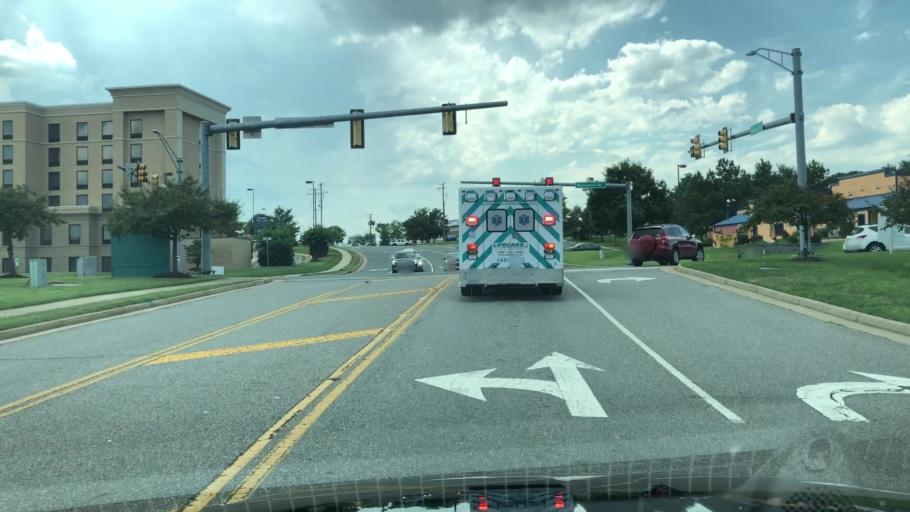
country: US
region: Virginia
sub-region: City of Fredericksburg
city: Fredericksburg
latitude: 38.2437
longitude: -77.4952
